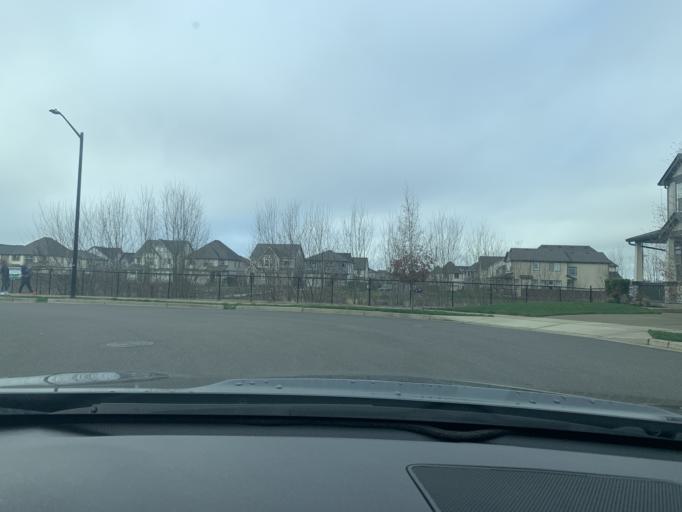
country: US
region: Oregon
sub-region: Washington County
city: North Plains
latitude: 45.5956
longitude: -122.9718
